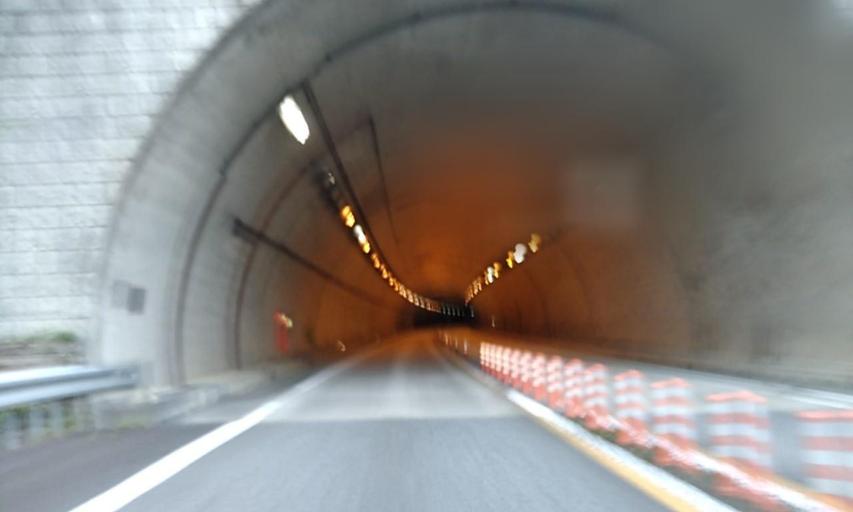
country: JP
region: Wakayama
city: Shingu
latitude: 33.6877
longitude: 135.9570
